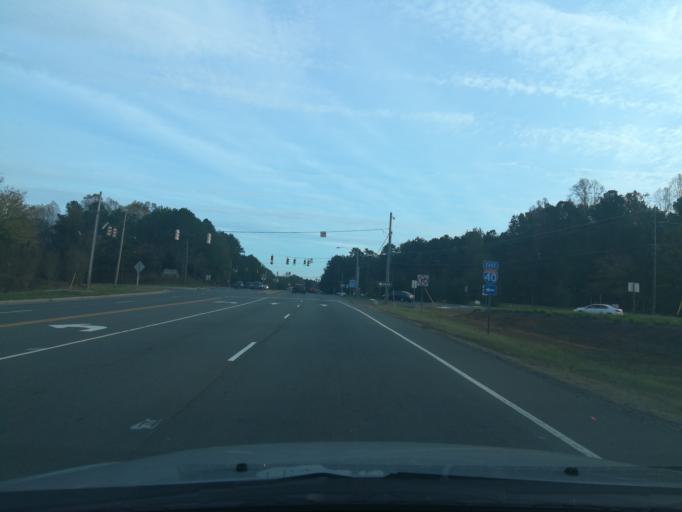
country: US
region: North Carolina
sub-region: Orange County
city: Chapel Hill
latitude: 35.9703
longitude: -79.0623
